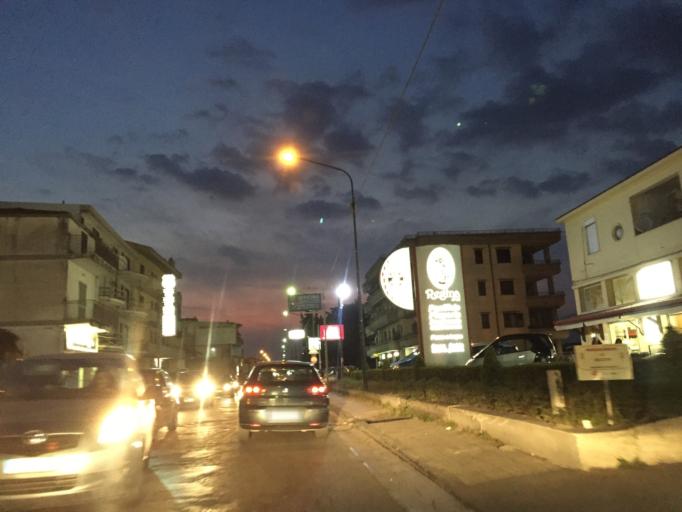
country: IT
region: Campania
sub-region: Provincia di Salerno
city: Pagani
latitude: 40.7477
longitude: 14.6025
